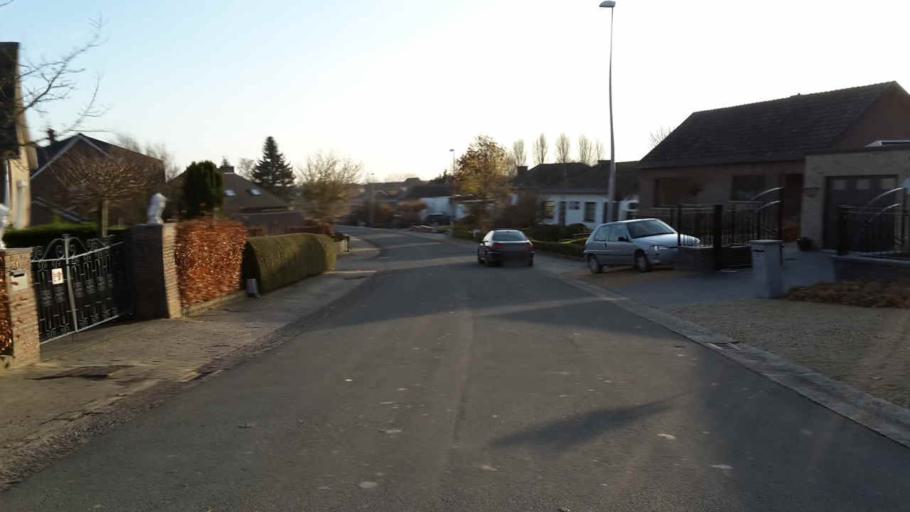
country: BE
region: Flanders
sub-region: Provincie Vlaams-Brabant
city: Hoegaarden
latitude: 50.8216
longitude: 4.8813
